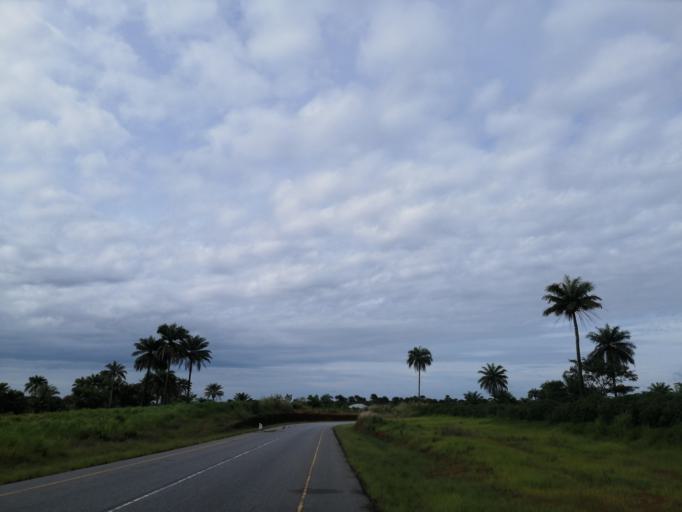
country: SL
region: Northern Province
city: Port Loko
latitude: 8.7885
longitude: -12.8481
